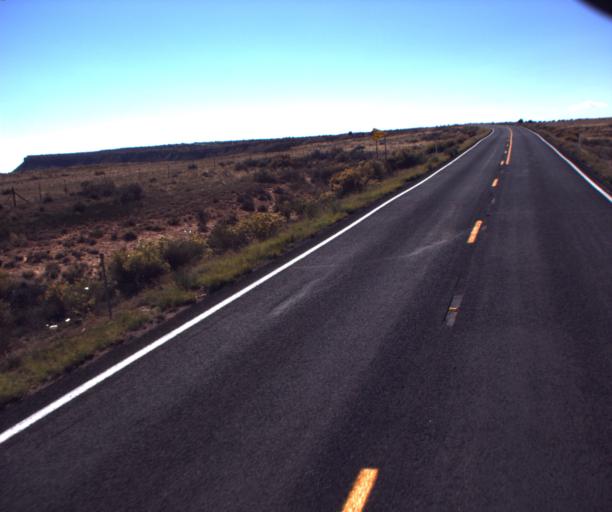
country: US
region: Arizona
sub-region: Coconino County
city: Tuba City
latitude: 35.9639
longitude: -110.8490
